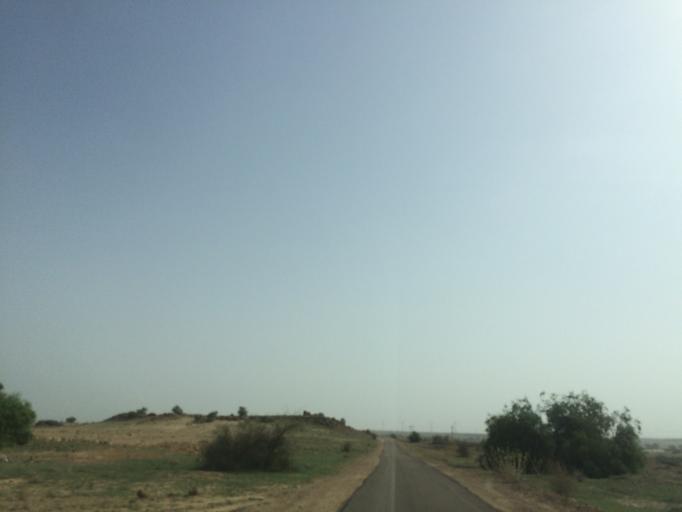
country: IN
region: Rajasthan
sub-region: Jaisalmer
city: Jaisalmer
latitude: 26.9057
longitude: 70.7836
